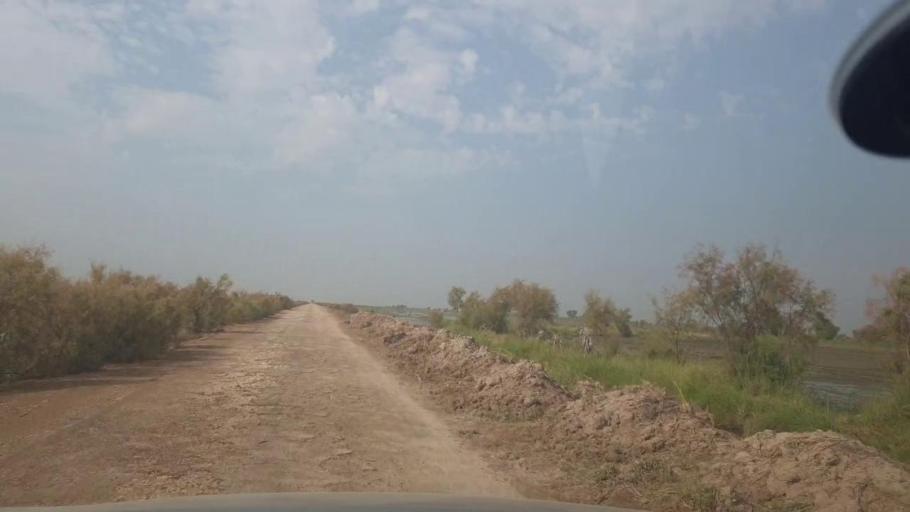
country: PK
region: Balochistan
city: Mehrabpur
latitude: 28.0267
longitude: 68.1452
